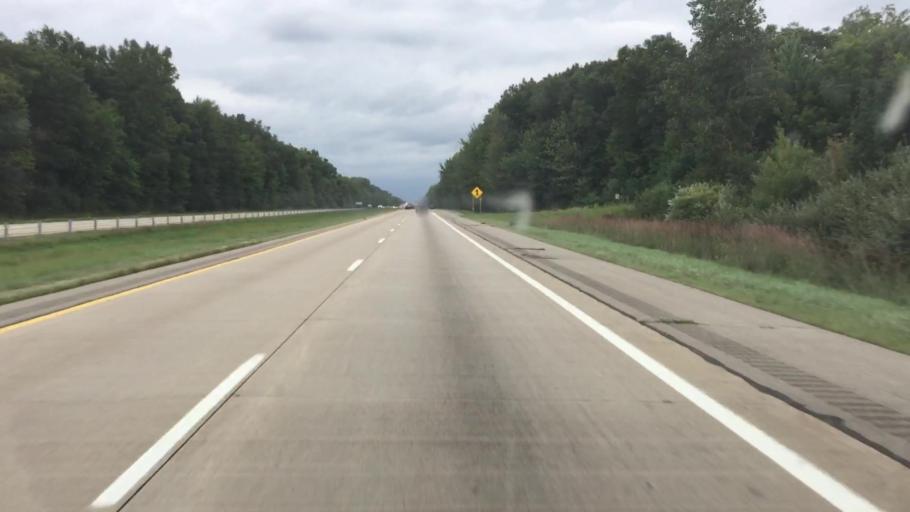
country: US
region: Michigan
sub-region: Monroe County
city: Dundee
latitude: 41.9291
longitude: -83.6626
